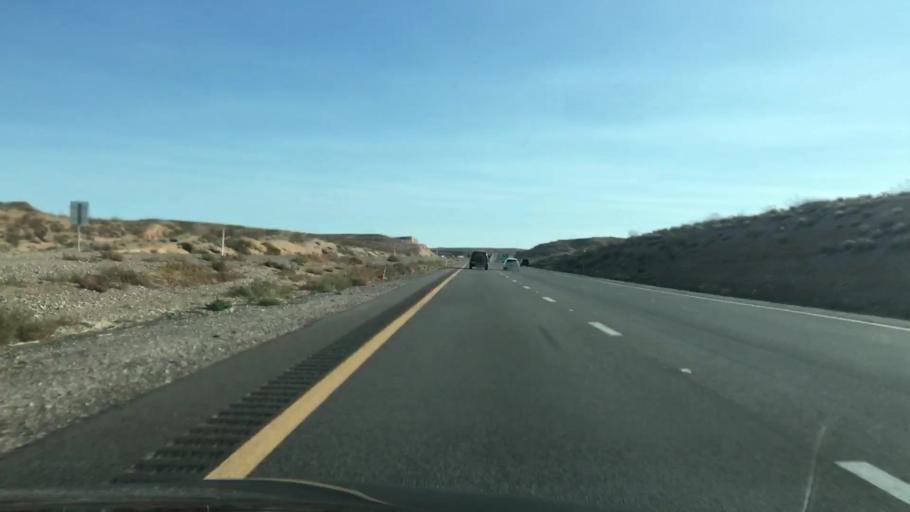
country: US
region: Nevada
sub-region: Clark County
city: Moapa Town
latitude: 36.6678
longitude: -114.5345
